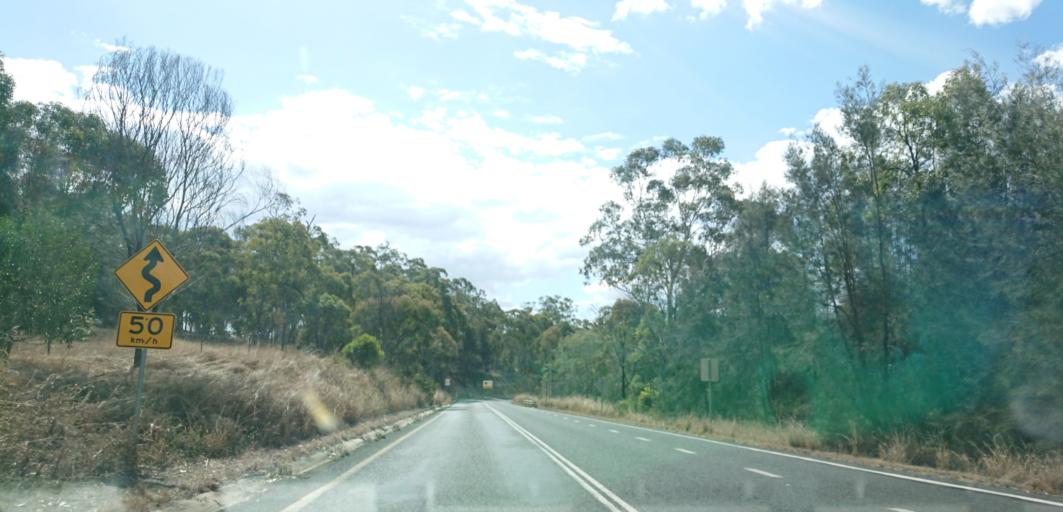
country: AU
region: Queensland
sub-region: Toowoomba
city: Top Camp
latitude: -27.7827
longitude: 152.0980
